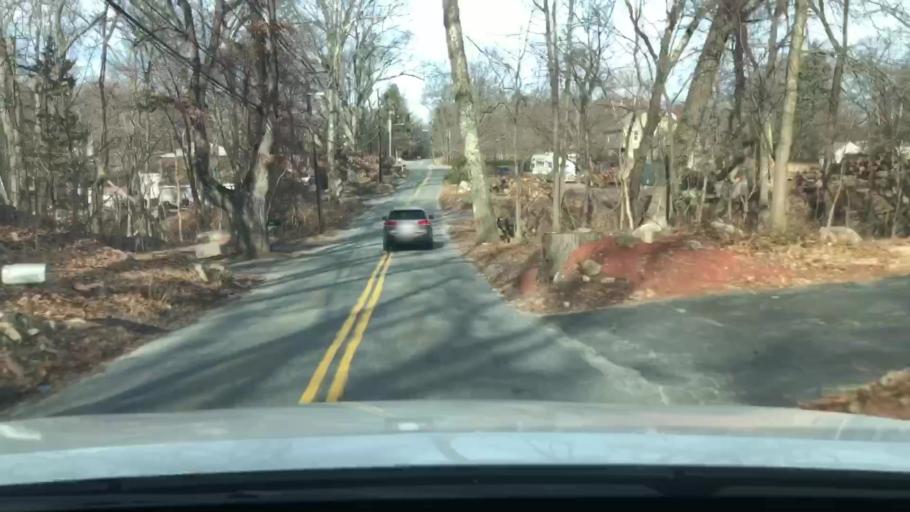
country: US
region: Massachusetts
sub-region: Worcester County
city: Milford
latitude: 42.1331
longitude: -71.4904
